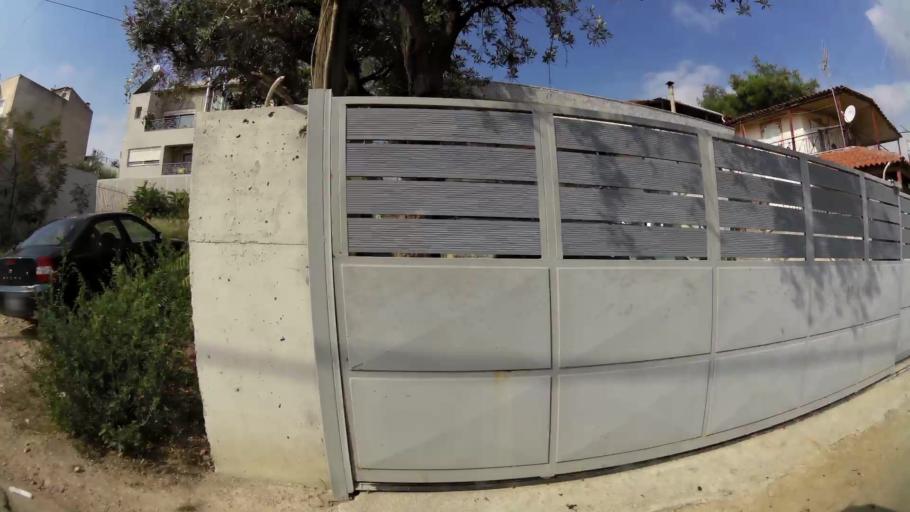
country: GR
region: Attica
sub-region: Nomarchia Dytikis Attikis
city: Zefyri
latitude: 38.0605
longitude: 23.7285
